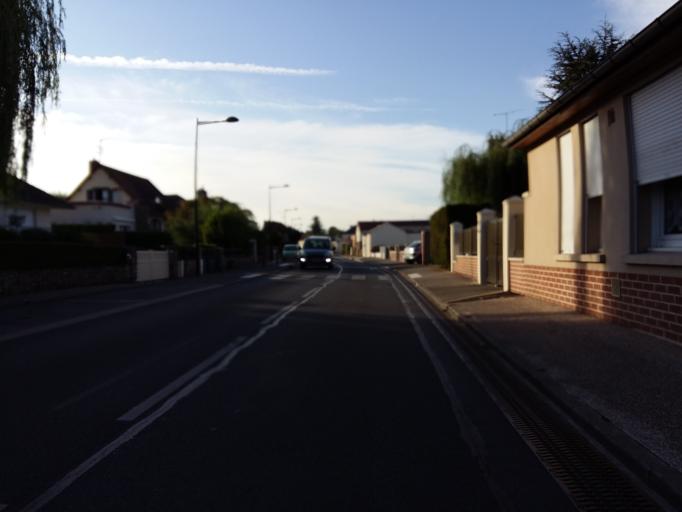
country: FR
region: Picardie
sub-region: Departement de la Somme
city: Camon
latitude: 49.8918
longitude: 2.3397
